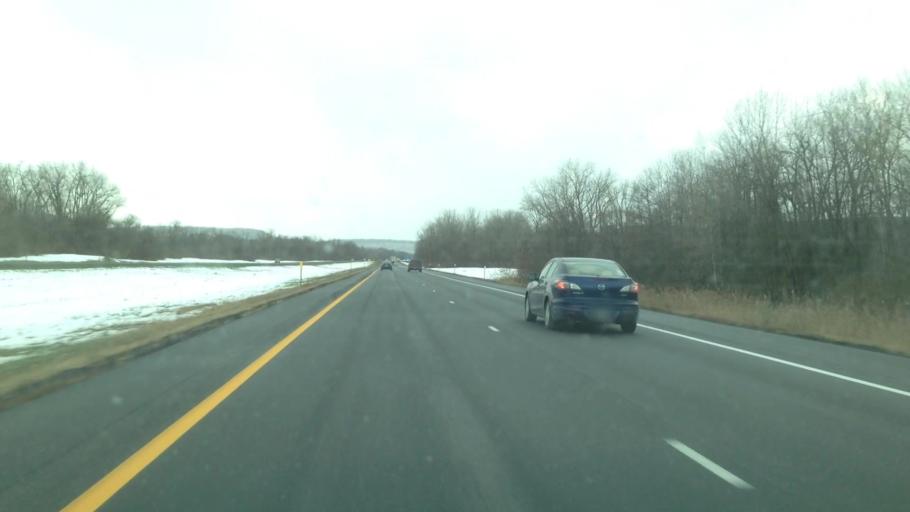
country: US
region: New York
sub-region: Montgomery County
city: Fonda
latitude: 42.9336
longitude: -74.4132
